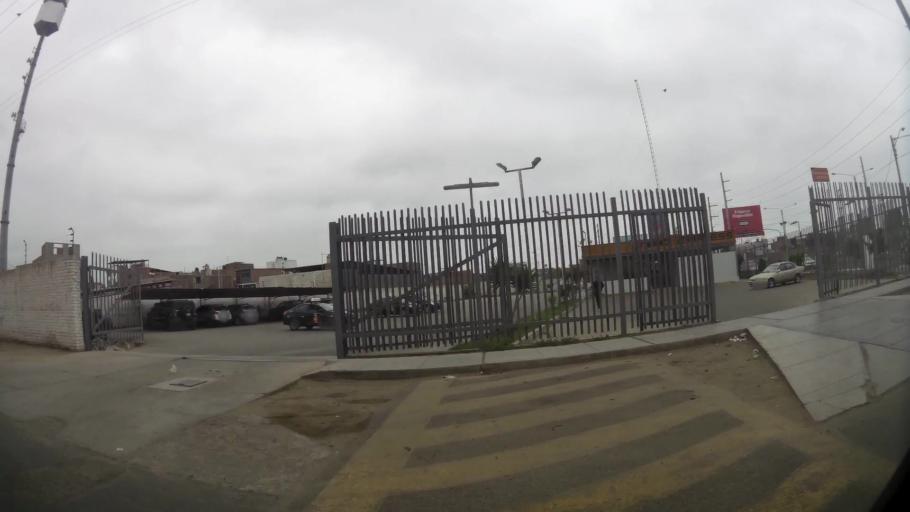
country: PE
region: La Libertad
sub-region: Provincia de Trujillo
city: Trujillo
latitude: -8.1060
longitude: -79.0463
